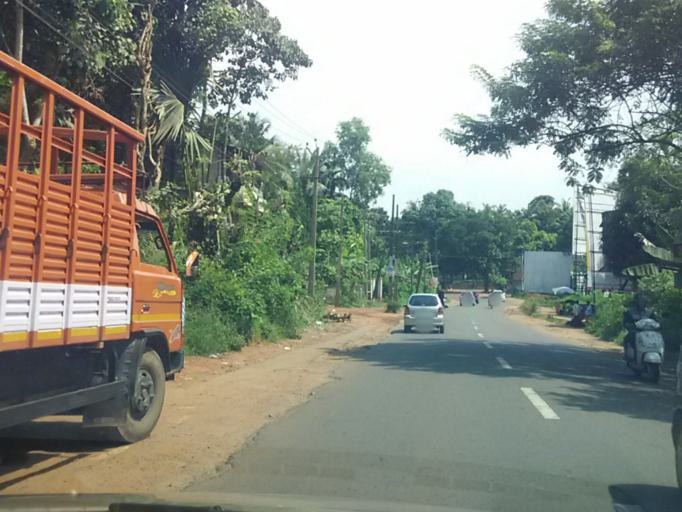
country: IN
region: Kerala
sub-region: Kozhikode
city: Kunnamangalam
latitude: 11.3104
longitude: 75.8821
